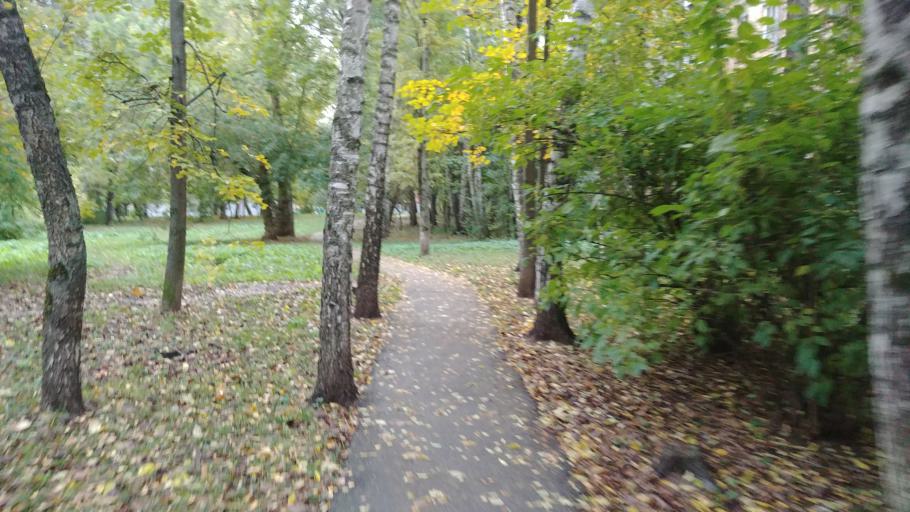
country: RU
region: Moscow
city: Golovinskiy
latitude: 55.8444
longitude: 37.4947
